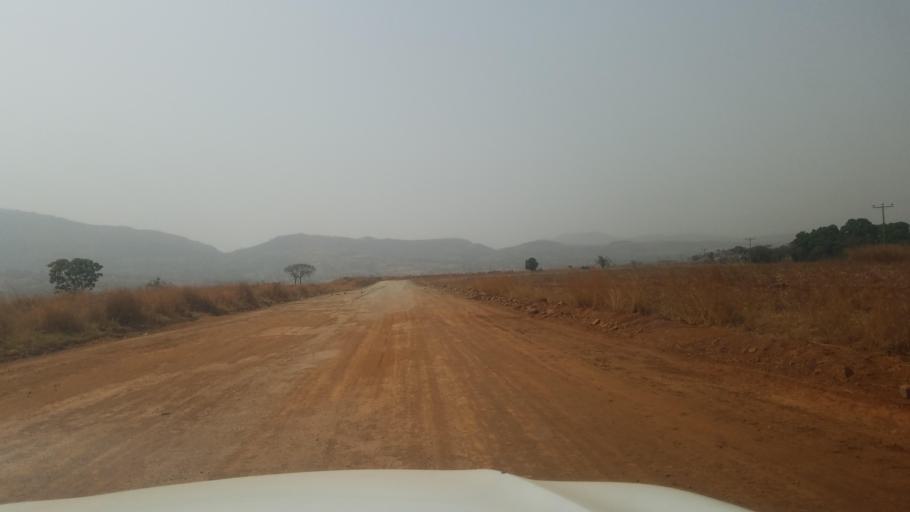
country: ET
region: Amhara
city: Bure
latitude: 10.9033
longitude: 36.4656
